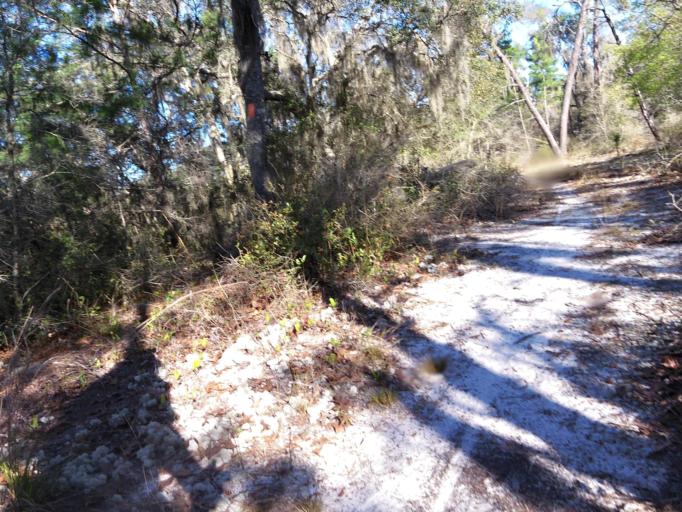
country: US
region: Florida
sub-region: Clay County
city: Keystone Heights
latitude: 29.8383
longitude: -82.0069
